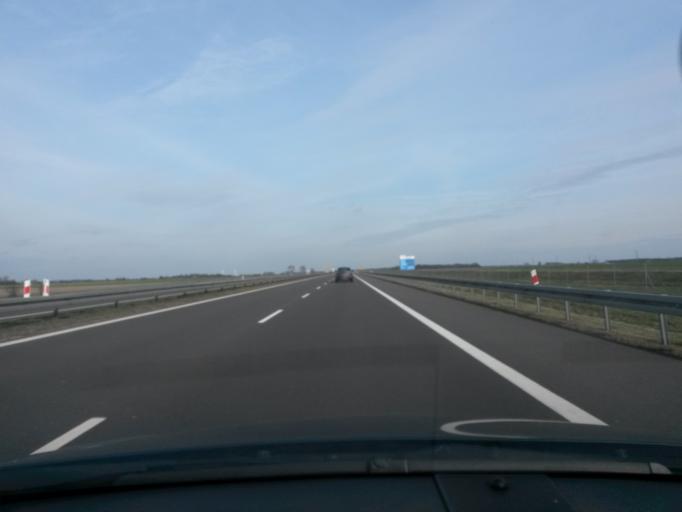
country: PL
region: Greater Poland Voivodeship
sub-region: Powiat sredzki
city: Dominowo
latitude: 52.3099
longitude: 17.3147
